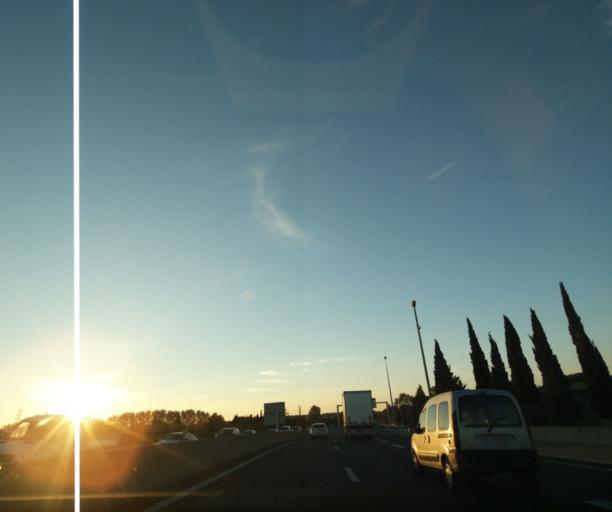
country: FR
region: Provence-Alpes-Cote d'Azur
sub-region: Departement des Bouches-du-Rhone
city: Salon-de-Provence
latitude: 43.6265
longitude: 5.1171
